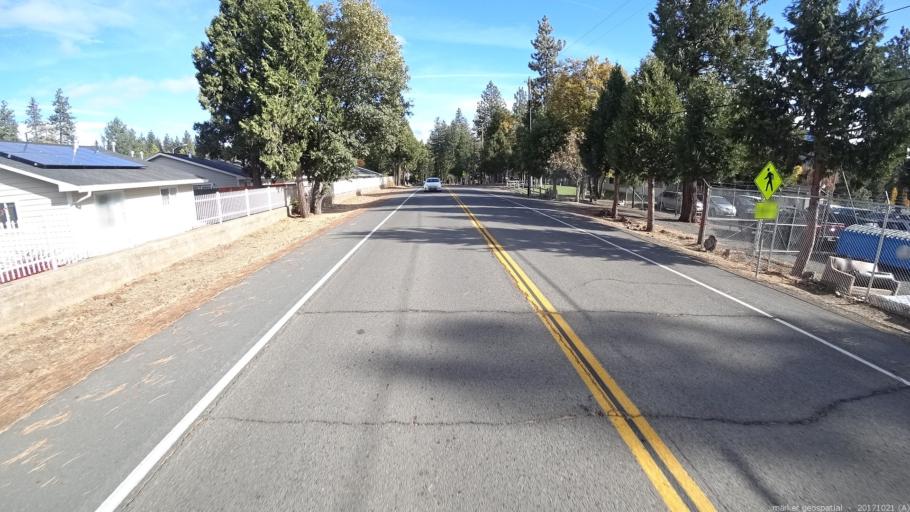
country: US
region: California
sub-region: Shasta County
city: Burney
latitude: 40.8766
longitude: -121.6735
